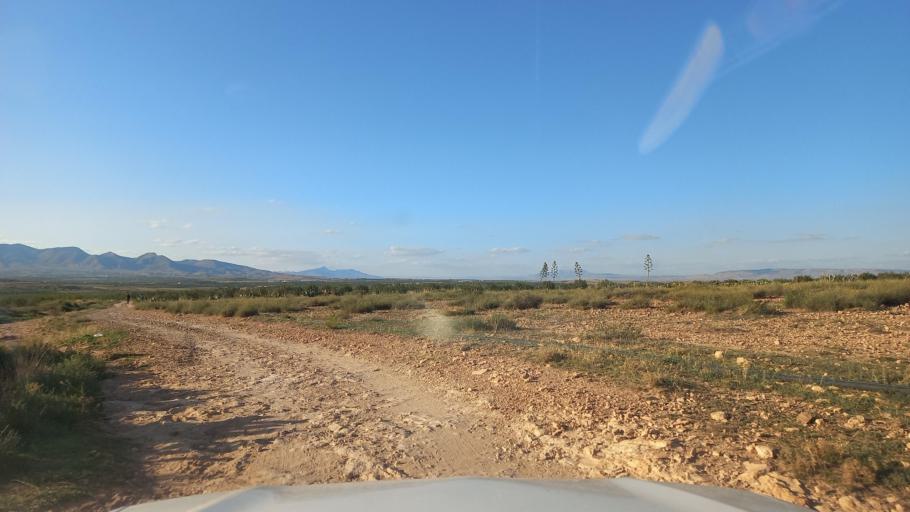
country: TN
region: Al Qasrayn
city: Sbiba
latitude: 35.3877
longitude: 9.1542
